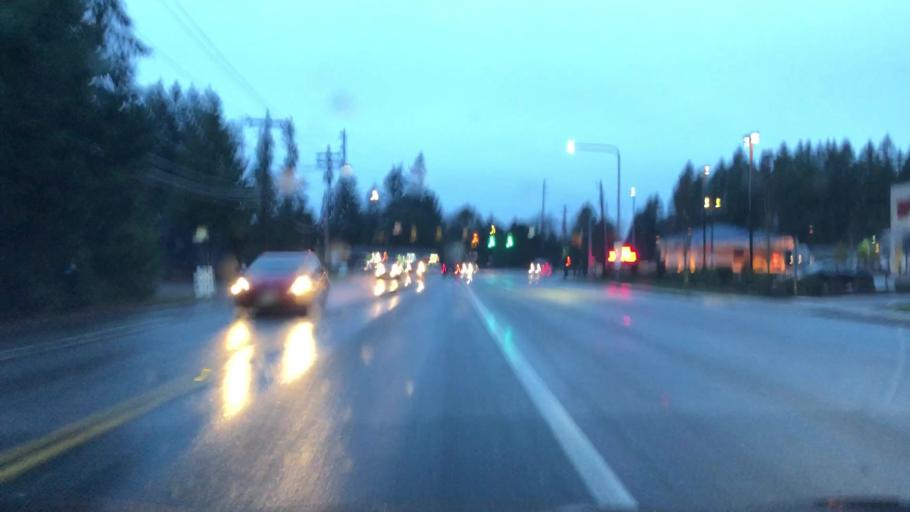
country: US
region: Washington
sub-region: King County
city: Cottage Lake
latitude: 47.7549
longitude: -122.0791
